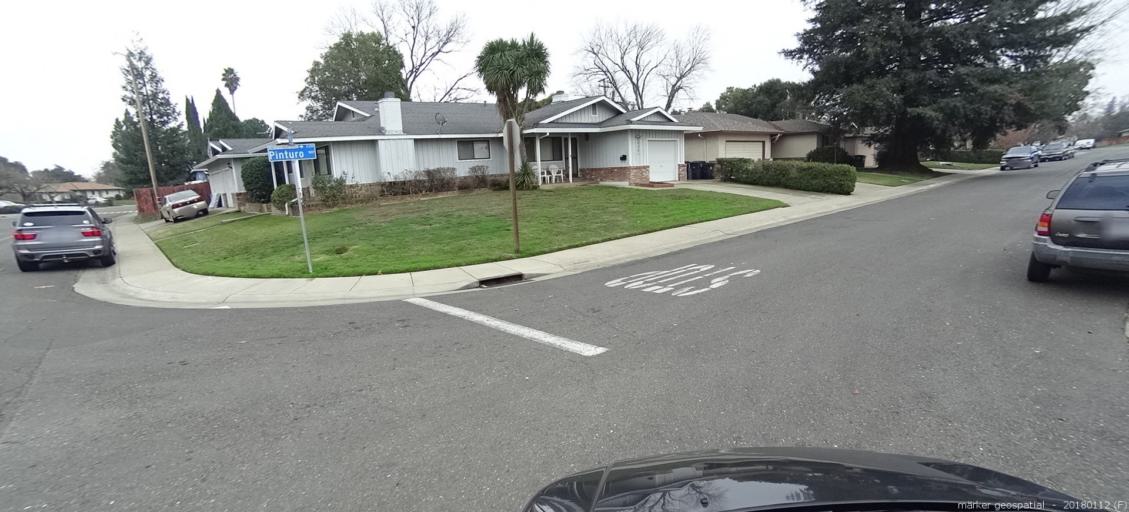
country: US
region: California
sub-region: Sacramento County
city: Rancho Cordova
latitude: 38.6122
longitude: -121.2846
